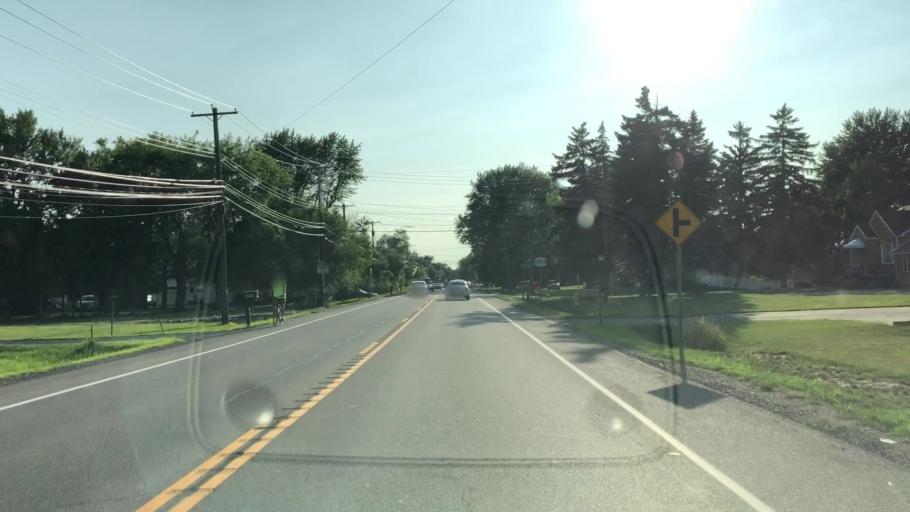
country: US
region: New York
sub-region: Erie County
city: Cheektowaga
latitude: 42.8566
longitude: -78.7388
